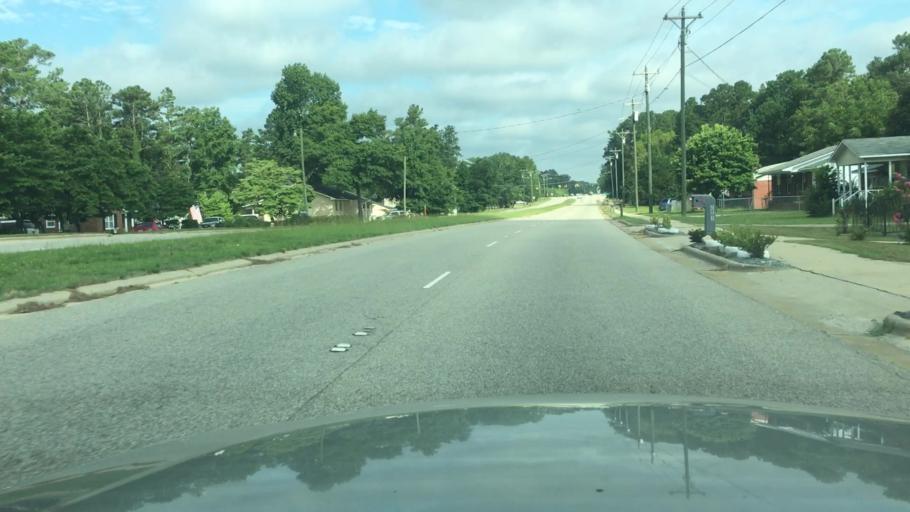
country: US
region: North Carolina
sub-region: Cumberland County
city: Hope Mills
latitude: 34.9923
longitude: -78.9626
